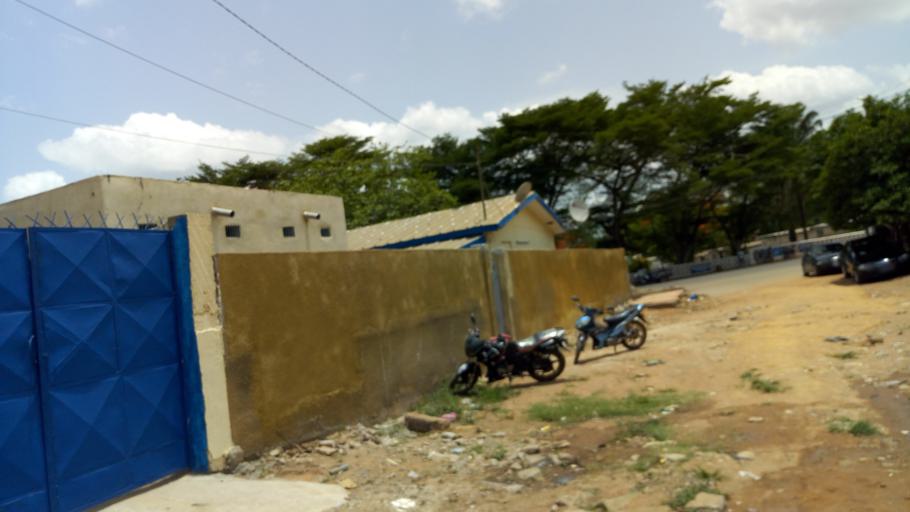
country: CI
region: Vallee du Bandama
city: Bouake
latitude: 7.6730
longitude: -5.0161
